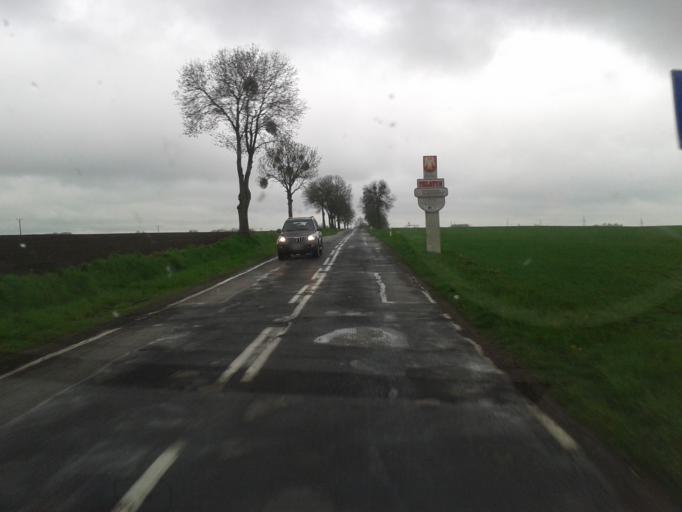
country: PL
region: Lublin Voivodeship
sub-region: Powiat hrubieszowski
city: Dolhobyczow
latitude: 50.5691
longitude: 23.9558
